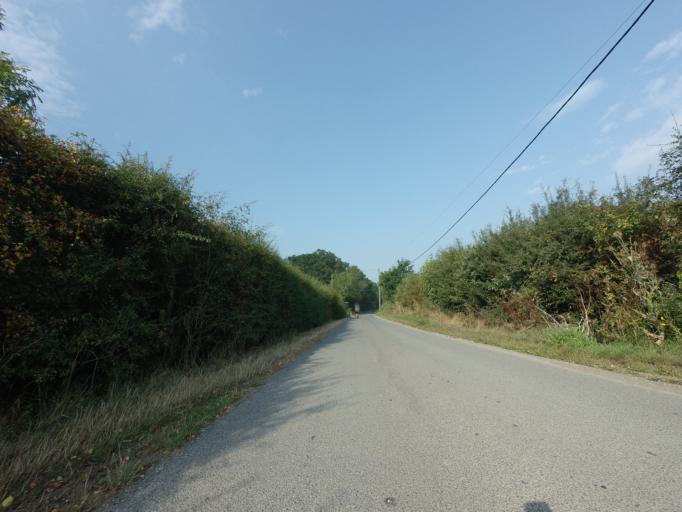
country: GB
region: England
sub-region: Kent
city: Tenterden
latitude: 51.1242
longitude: 0.6686
